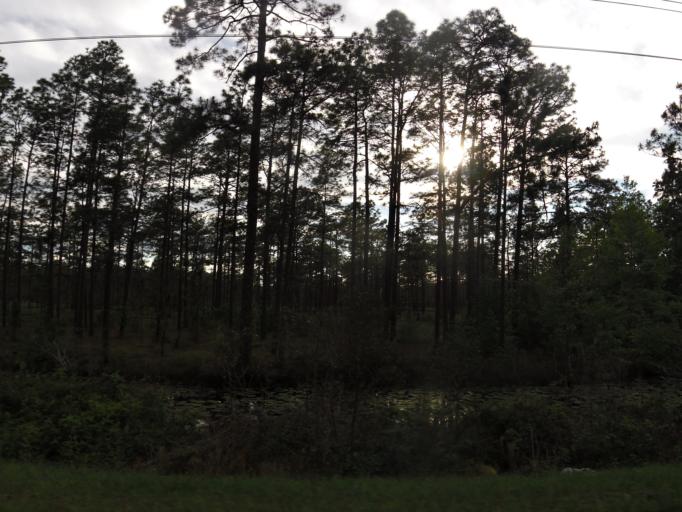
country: US
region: South Carolina
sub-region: Jasper County
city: Hardeeville
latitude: 32.3496
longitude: -81.0929
